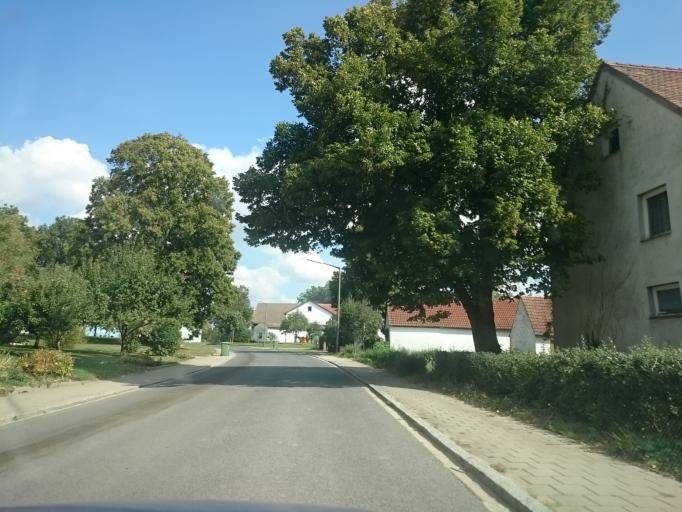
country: DE
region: Bavaria
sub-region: Upper Palatinate
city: Freystadt
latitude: 49.1474
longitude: 11.2972
